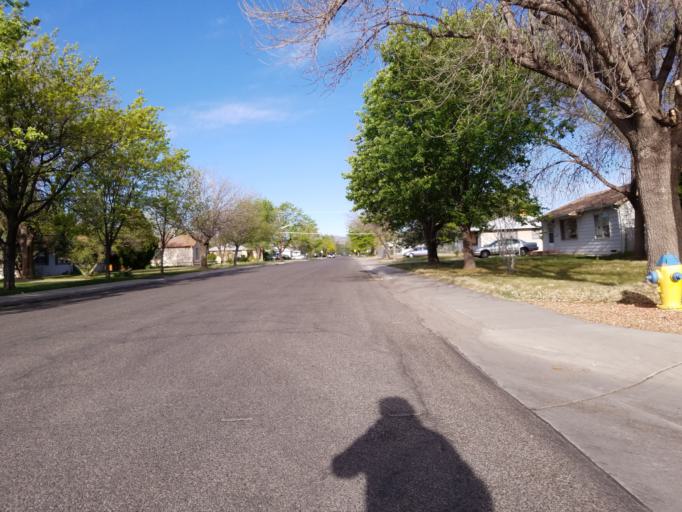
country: US
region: Colorado
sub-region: Mesa County
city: Grand Junction
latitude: 39.0810
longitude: -108.5419
